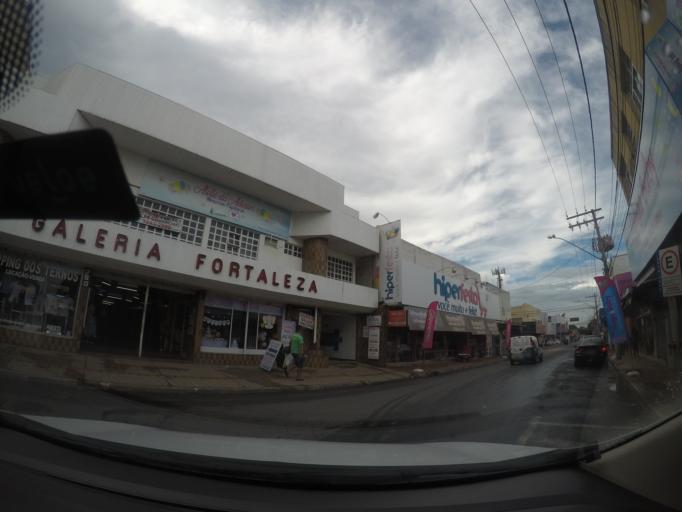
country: BR
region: Goias
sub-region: Goiania
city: Goiania
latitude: -16.6698
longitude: -49.2934
